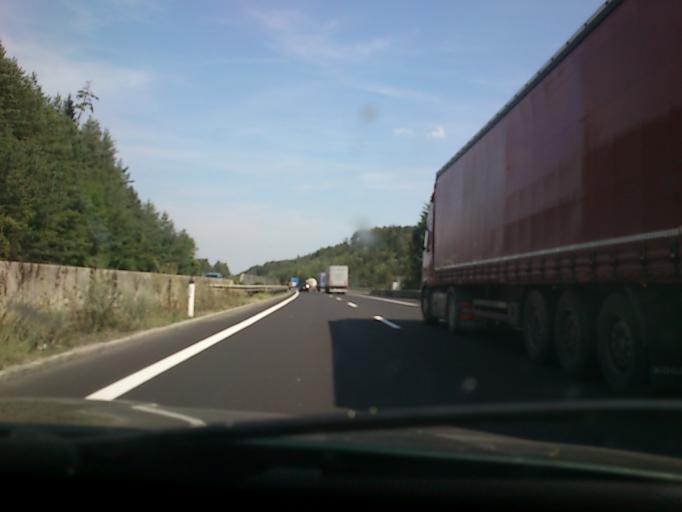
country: AT
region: Lower Austria
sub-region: Politischer Bezirk Neunkirchen
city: Seebenstein
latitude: 47.6955
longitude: 16.1302
